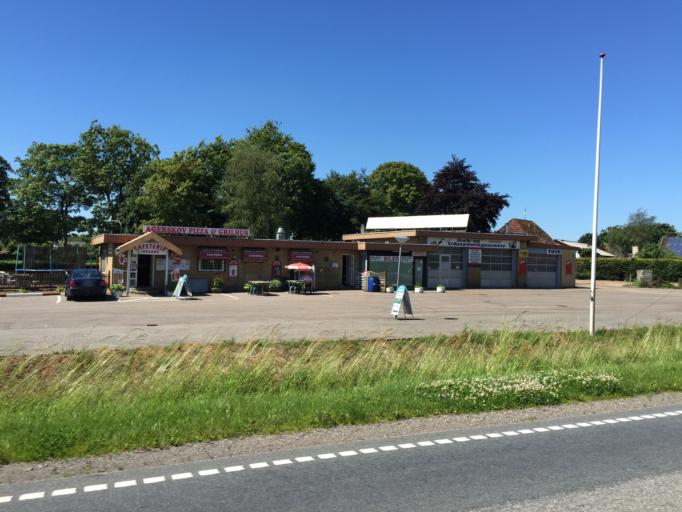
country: DK
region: South Denmark
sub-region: Tonder Kommune
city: Toftlund
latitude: 55.1309
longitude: 9.1398
